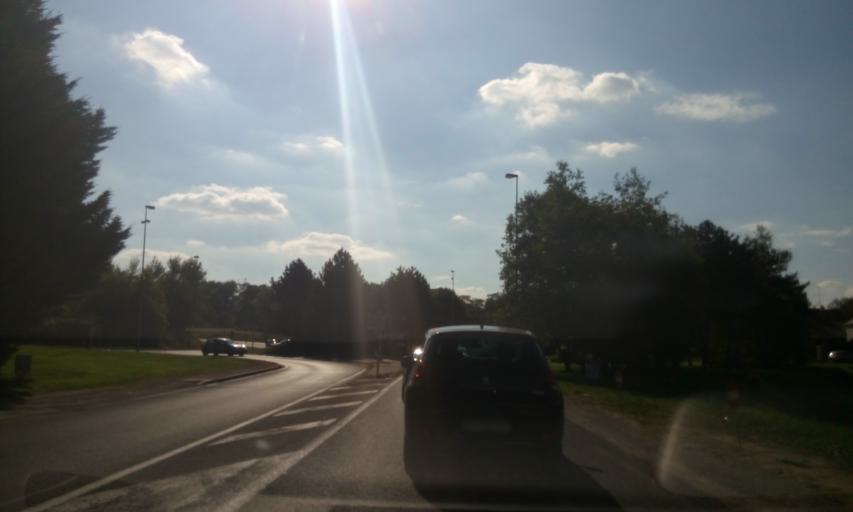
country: FR
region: Centre
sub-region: Departement d'Indre-et-Loire
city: Charge
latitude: 47.4036
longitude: 1.0189
